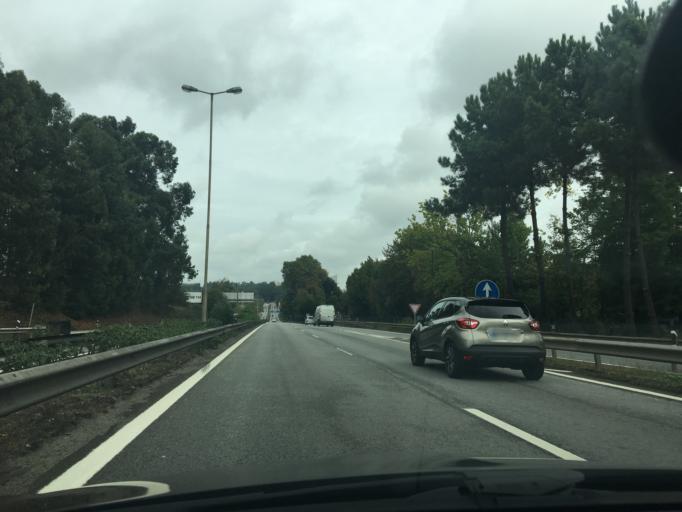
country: PT
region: Porto
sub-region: Maia
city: Leca do Bailio
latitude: 41.2118
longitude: -8.6272
